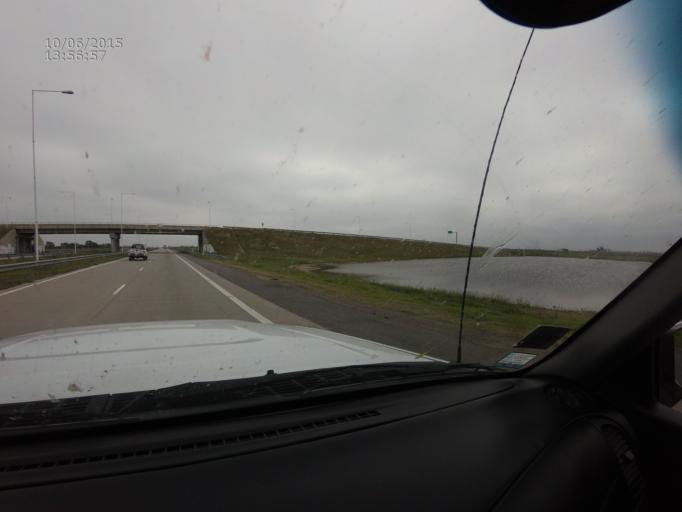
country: AR
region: Cordoba
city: Morrison
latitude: -32.5612
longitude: -62.8197
